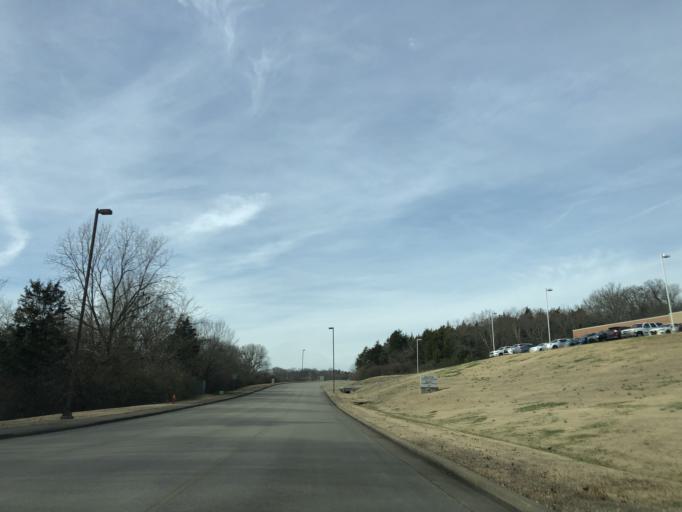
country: US
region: Tennessee
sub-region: Davidson County
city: Nashville
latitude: 36.2129
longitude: -86.7429
